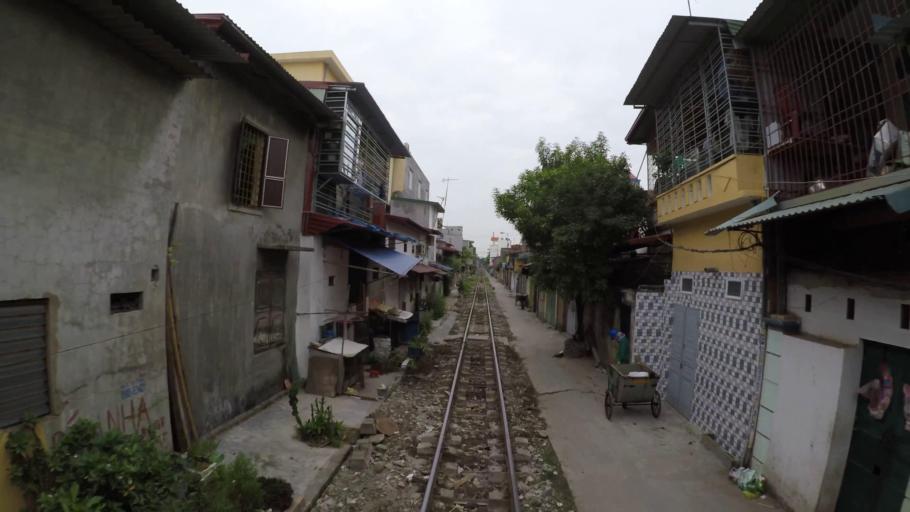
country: VN
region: Hai Phong
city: Haiphong
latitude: 20.8641
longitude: 106.6597
